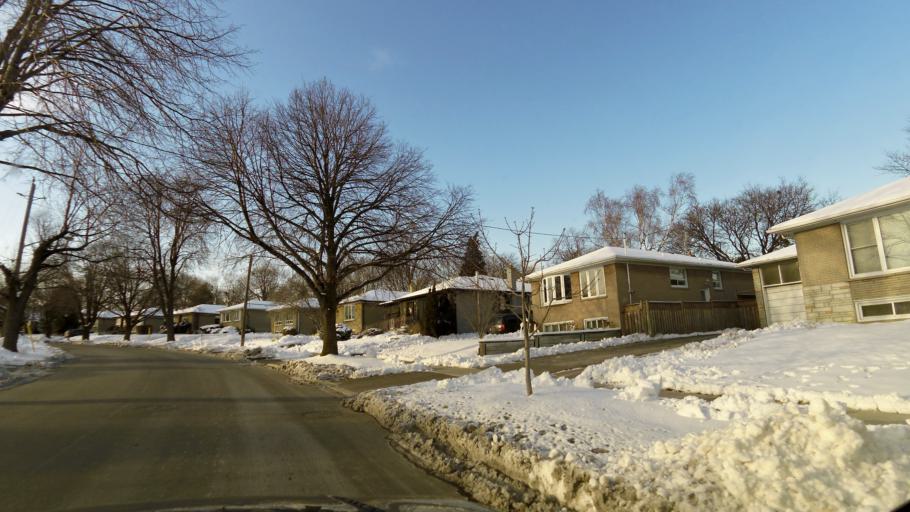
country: CA
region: Ontario
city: Etobicoke
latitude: 43.6654
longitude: -79.5820
